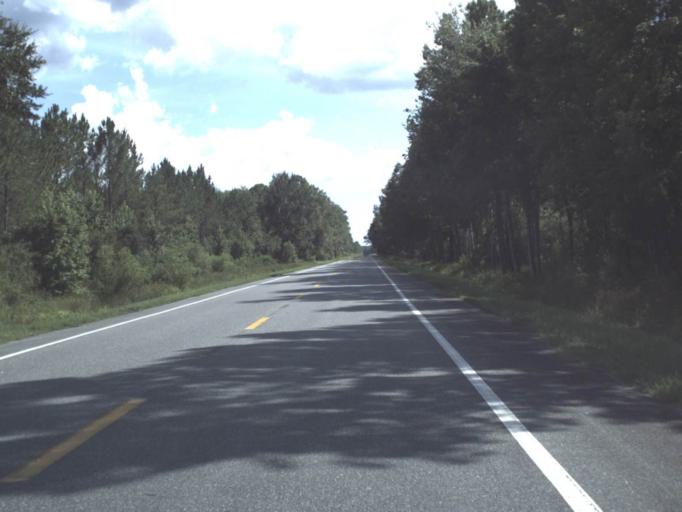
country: US
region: Florida
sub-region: Lafayette County
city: Mayo
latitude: 29.8979
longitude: -83.2971
